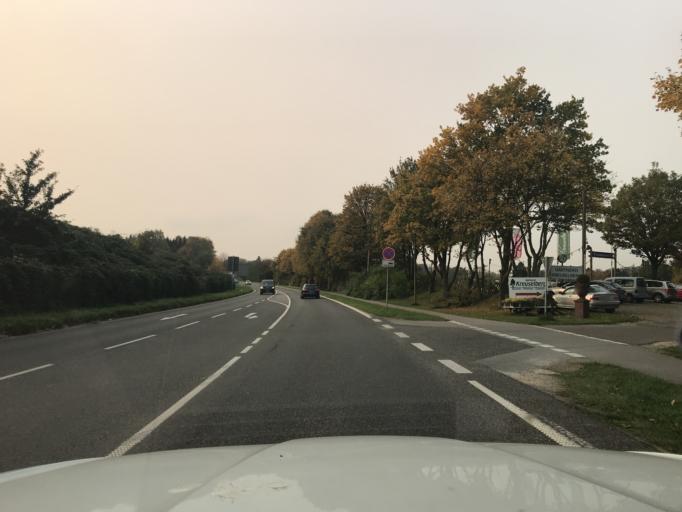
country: DE
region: North Rhine-Westphalia
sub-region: Regierungsbezirk Dusseldorf
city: Muelheim (Ruhr)
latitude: 51.4079
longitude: 6.9477
